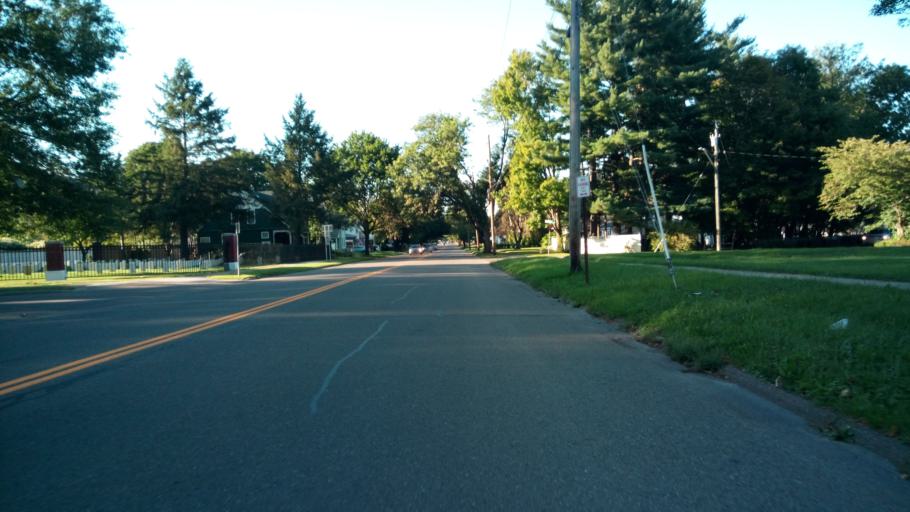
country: US
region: New York
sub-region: Chemung County
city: Elmira Heights
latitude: 42.1109
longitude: -76.8263
